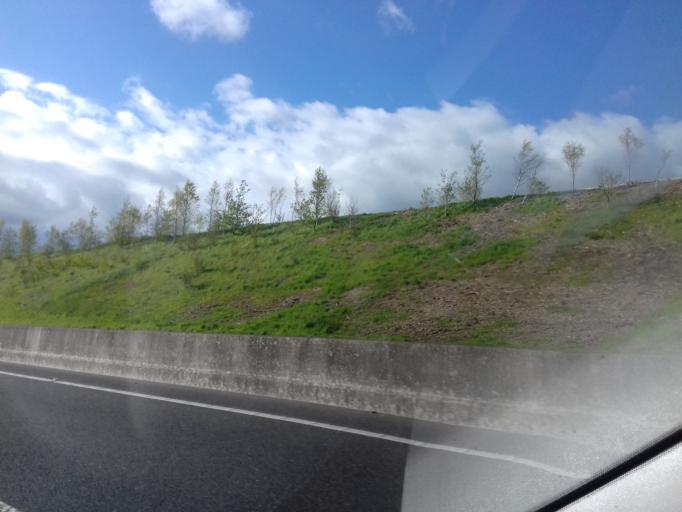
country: IE
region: Leinster
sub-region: Kilkenny
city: Mooncoin
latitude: 52.4052
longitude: -7.1951
